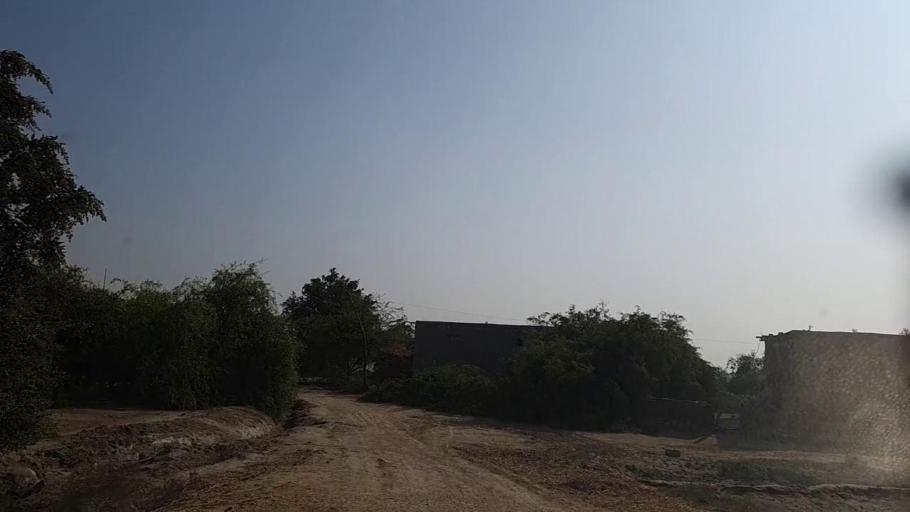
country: PK
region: Sindh
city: Mirpur Batoro
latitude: 24.6123
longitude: 68.2842
